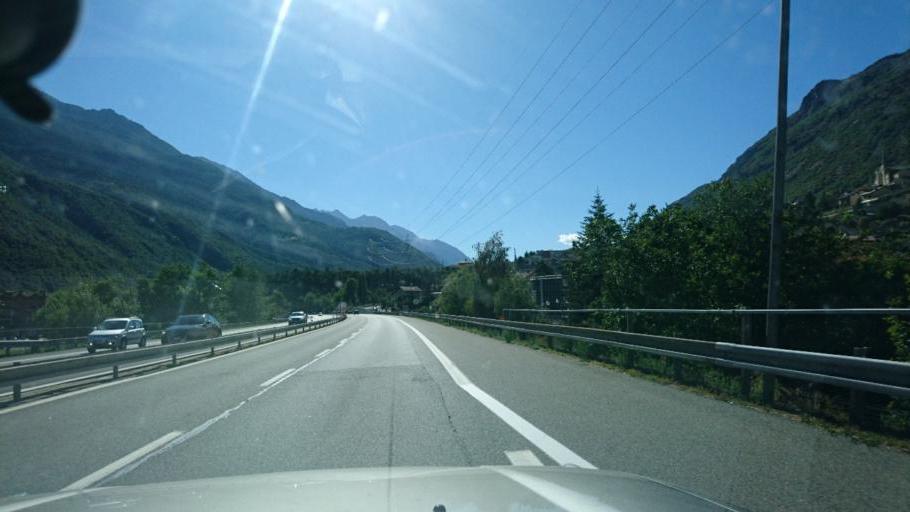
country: IT
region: Aosta Valley
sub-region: Valle d'Aosta
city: Chatillon
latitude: 45.7473
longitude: 7.6182
